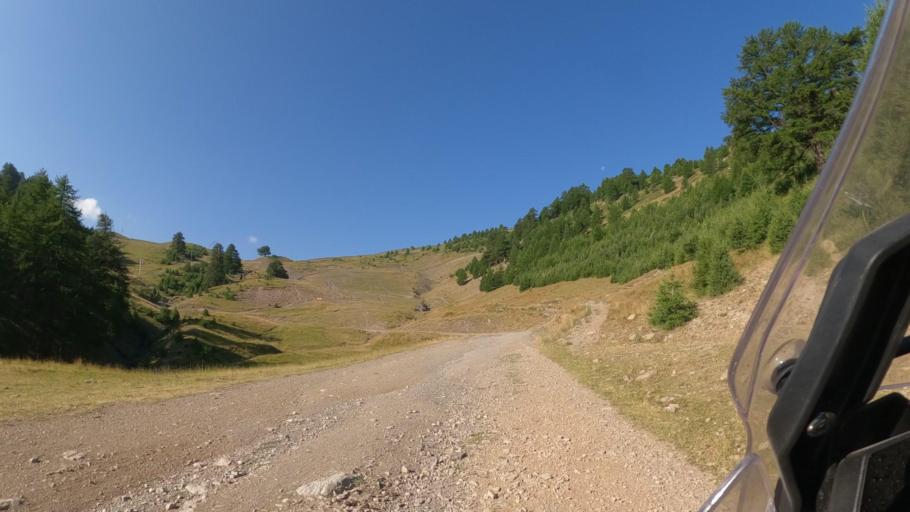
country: FR
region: Provence-Alpes-Cote d'Azur
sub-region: Departement des Hautes-Alpes
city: Guillestre
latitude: 44.6102
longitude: 6.6243
